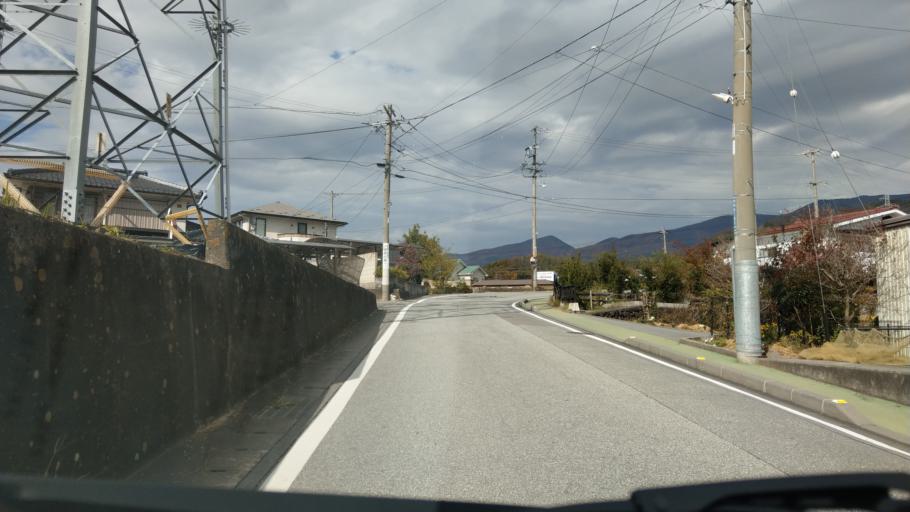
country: JP
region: Nagano
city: Komoro
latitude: 36.3346
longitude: 138.4160
